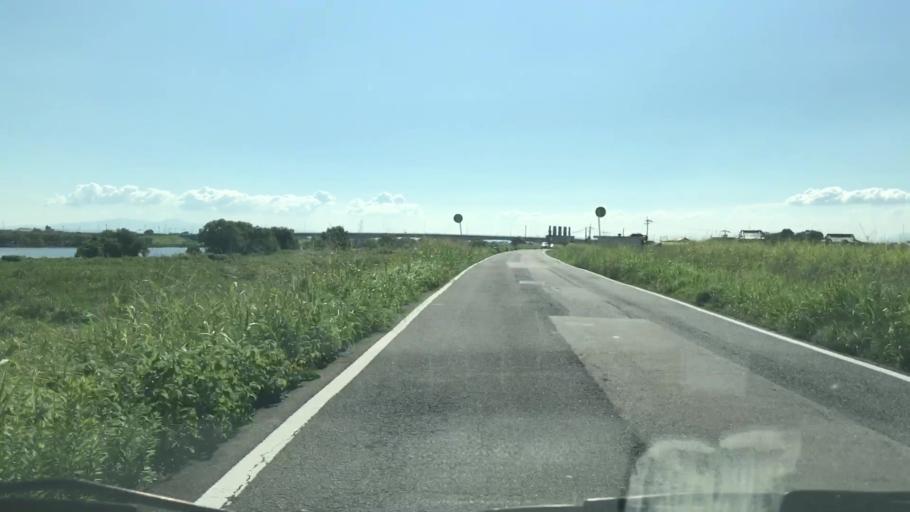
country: JP
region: Saga Prefecture
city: Kanzakimachi-kanzaki
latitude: 33.2740
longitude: 130.4391
